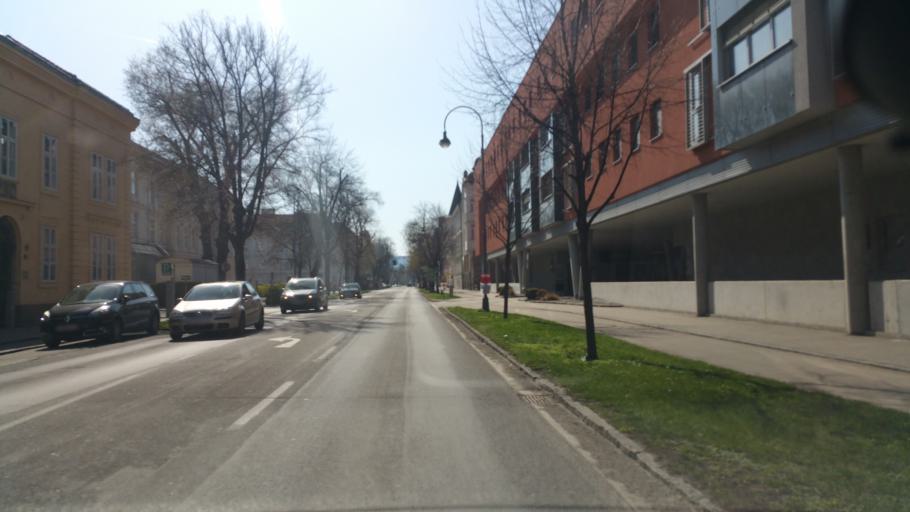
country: AT
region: Lower Austria
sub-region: Politischer Bezirk Krems
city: Weinzierl bei Krems
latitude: 48.4089
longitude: 15.6010
